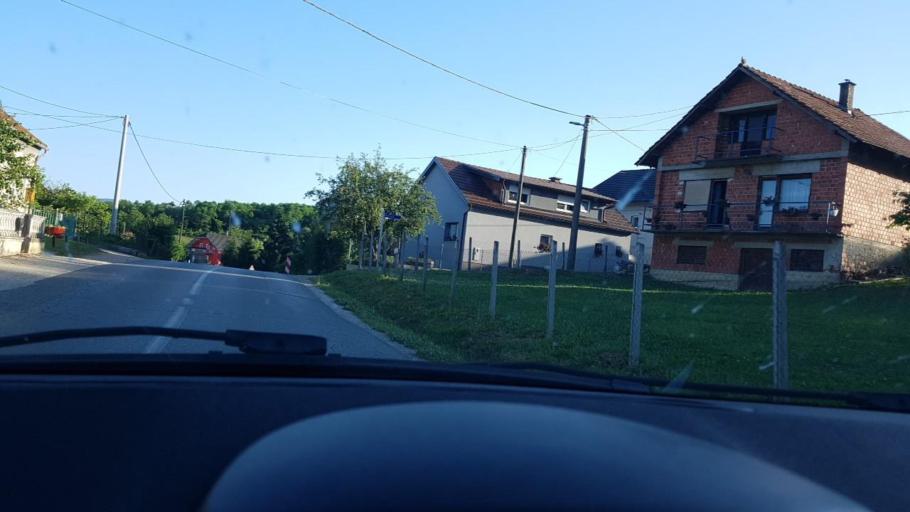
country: HR
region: Krapinsko-Zagorska
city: Bedekovcina
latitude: 46.0551
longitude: 16.0003
